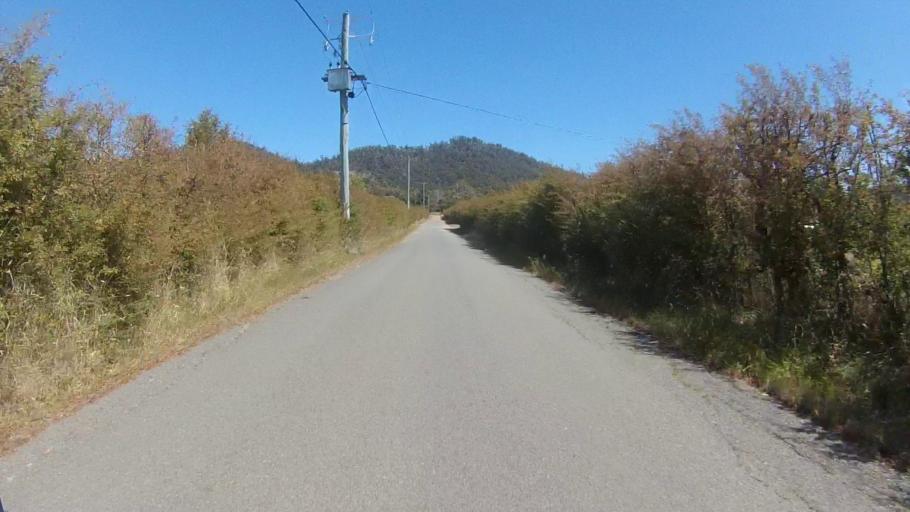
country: AU
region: Tasmania
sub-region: Clarence
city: Cambridge
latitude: -42.8448
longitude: 147.4585
